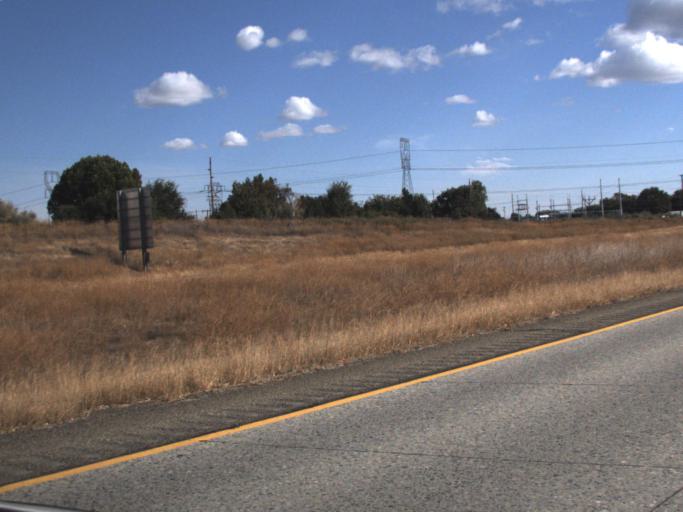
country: US
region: Washington
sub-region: Yakima County
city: Sunnyside
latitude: 46.2952
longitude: -119.9575
